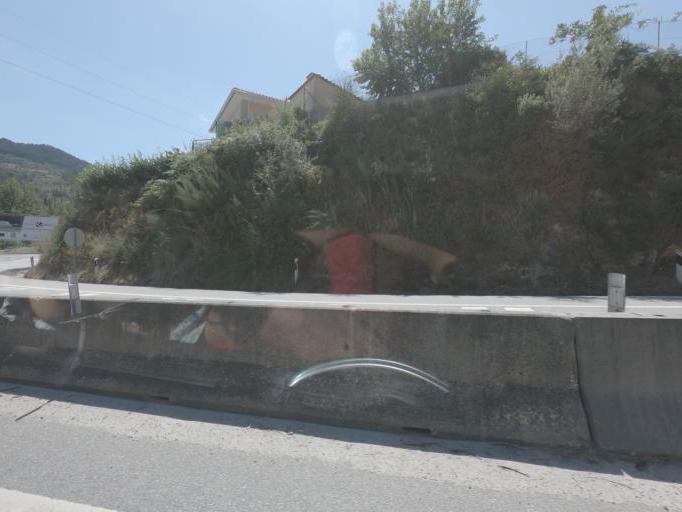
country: PT
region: Porto
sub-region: Amarante
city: Amarante
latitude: 41.2544
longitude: -8.0458
